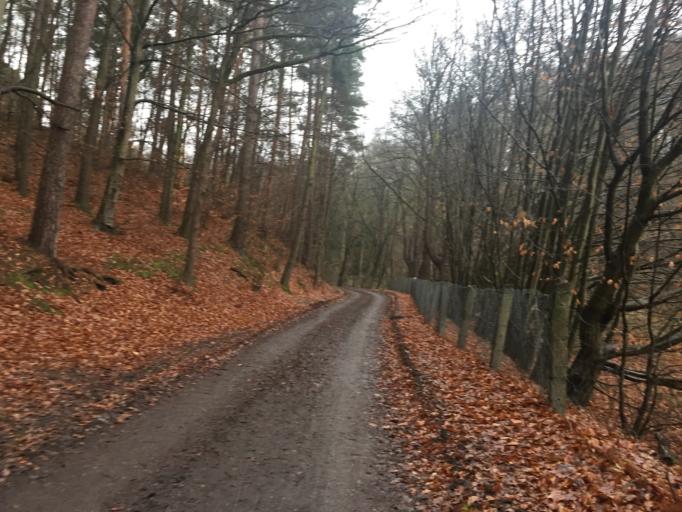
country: DE
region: Thuringia
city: Stadtroda
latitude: 50.8569
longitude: 11.7393
